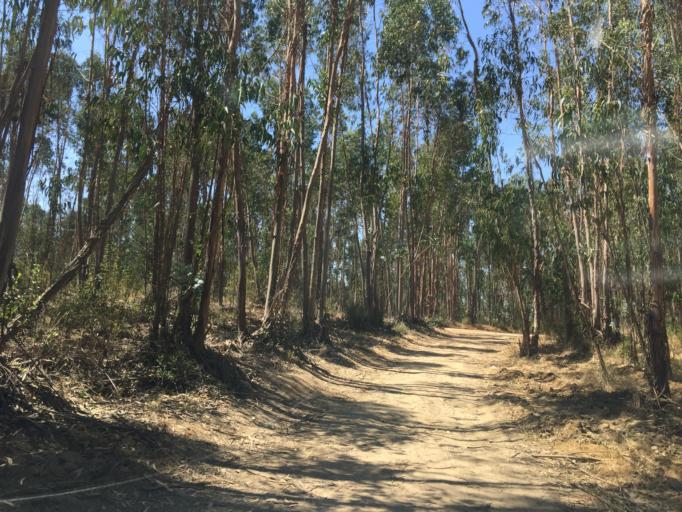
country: PT
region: Santarem
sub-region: Tomar
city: Tomar
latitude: 39.6079
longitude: -8.3563
